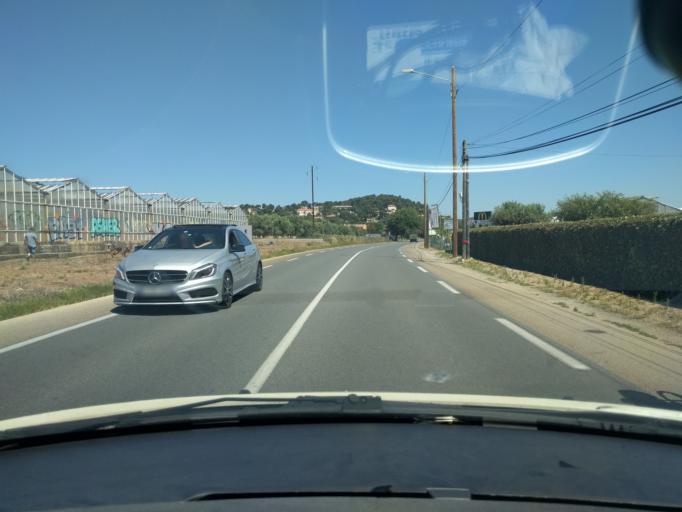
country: FR
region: Provence-Alpes-Cote d'Azur
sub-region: Departement du Var
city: Hyeres
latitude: 43.0866
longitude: 6.1288
